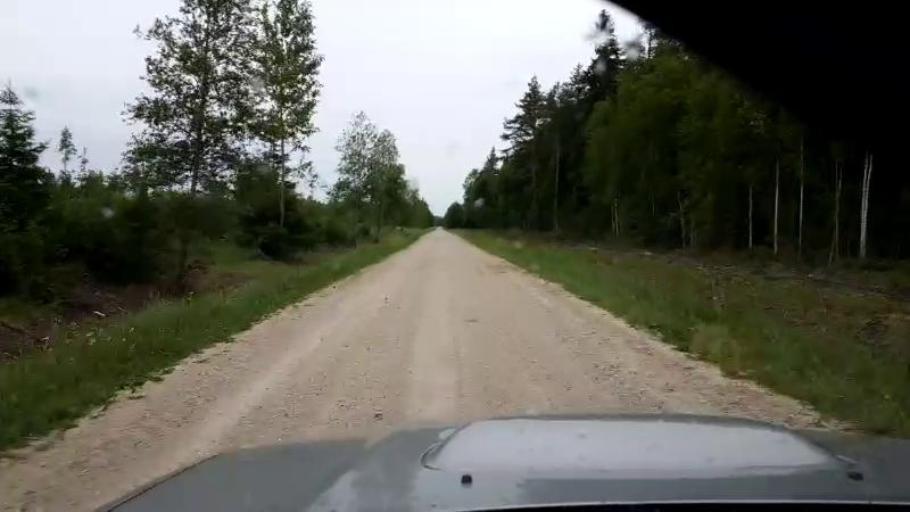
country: EE
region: Paernumaa
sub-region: Halinga vald
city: Parnu-Jaagupi
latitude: 58.5390
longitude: 24.5959
